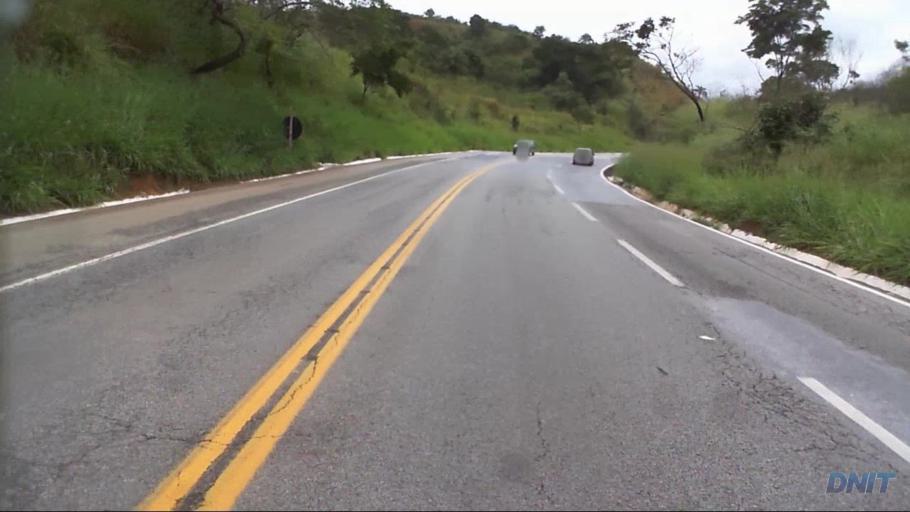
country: BR
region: Minas Gerais
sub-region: Barao De Cocais
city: Barao de Cocais
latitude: -19.8352
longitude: -43.3695
